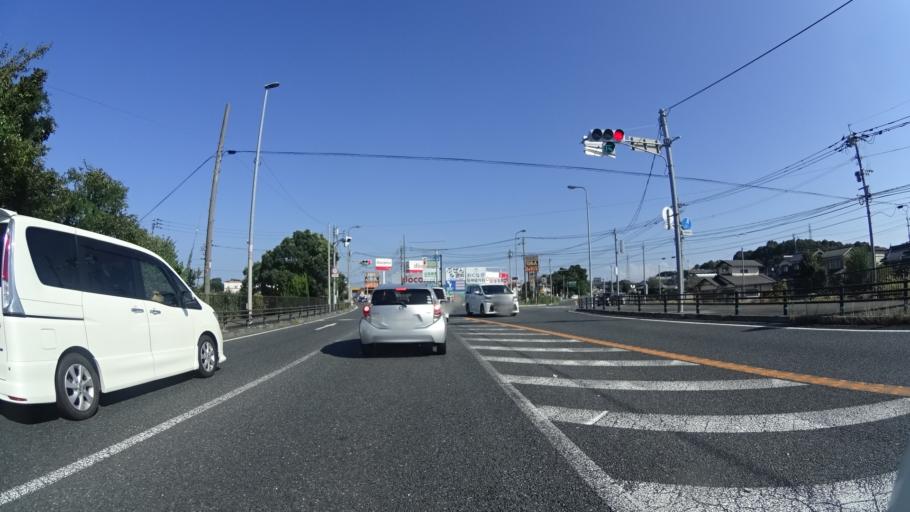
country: JP
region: Fukuoka
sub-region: Buzen-shi
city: Buzen
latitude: 33.6166
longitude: 131.0991
